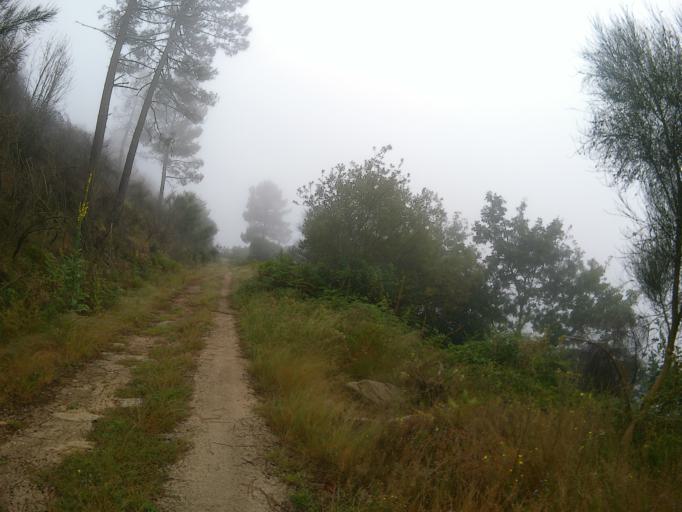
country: PT
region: Viana do Castelo
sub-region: Ponte de Lima
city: Ponte de Lima
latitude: 41.7038
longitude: -8.6042
